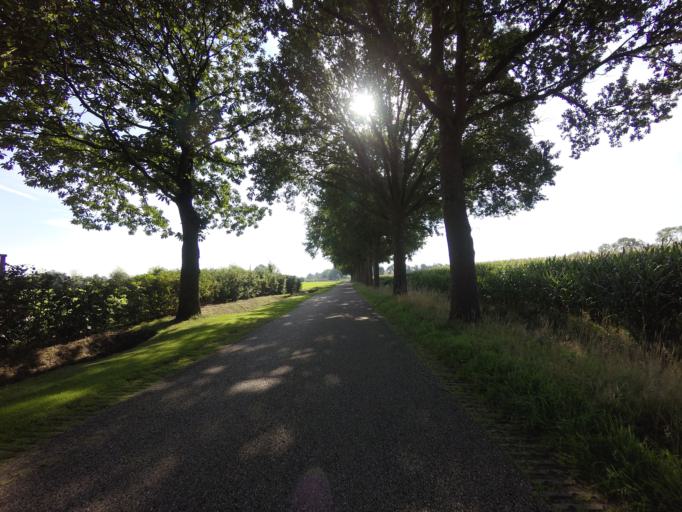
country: NL
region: Gelderland
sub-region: Oost Gelre
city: Lichtenvoorde
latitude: 52.0041
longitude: 6.5051
